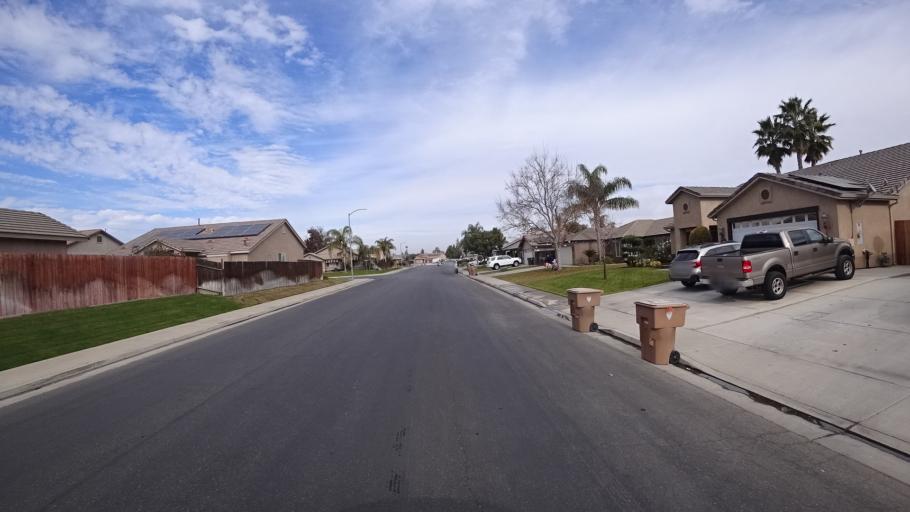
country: US
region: California
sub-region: Kern County
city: Rosedale
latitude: 35.3924
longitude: -119.1317
